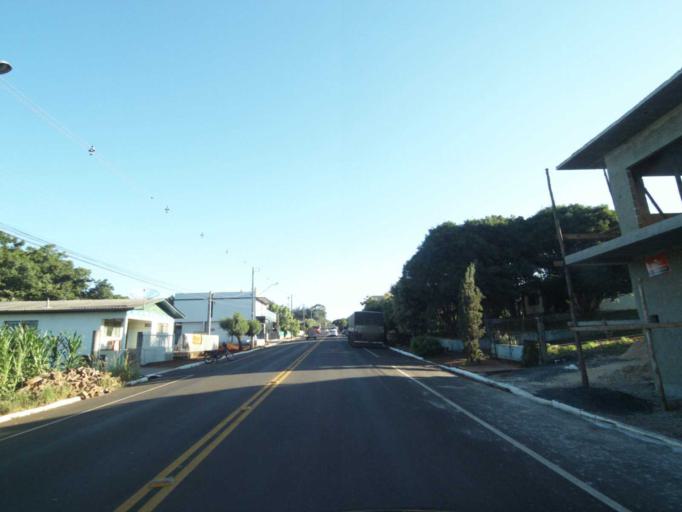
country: BR
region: Parana
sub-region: Coronel Vivida
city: Coronel Vivida
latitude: -25.9713
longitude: -52.8154
